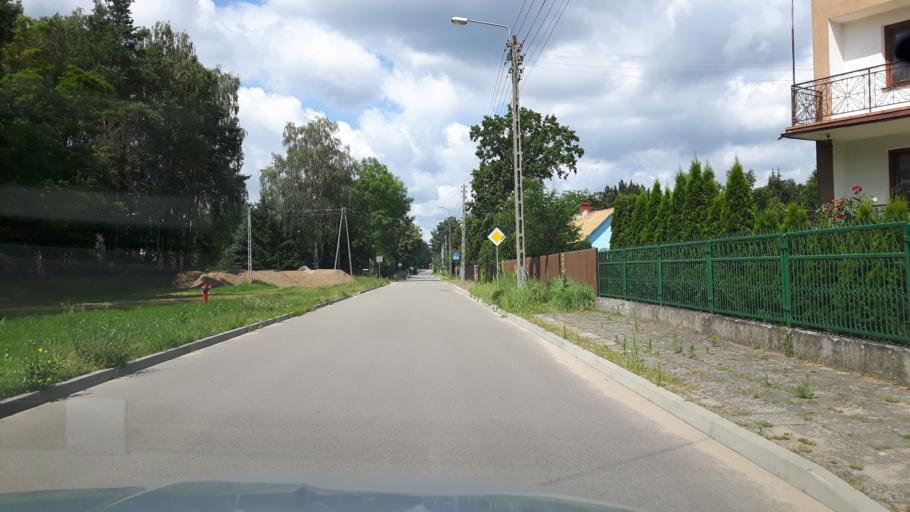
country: PL
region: Masovian Voivodeship
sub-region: Powiat ostrowski
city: Brok
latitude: 52.6997
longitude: 21.8537
